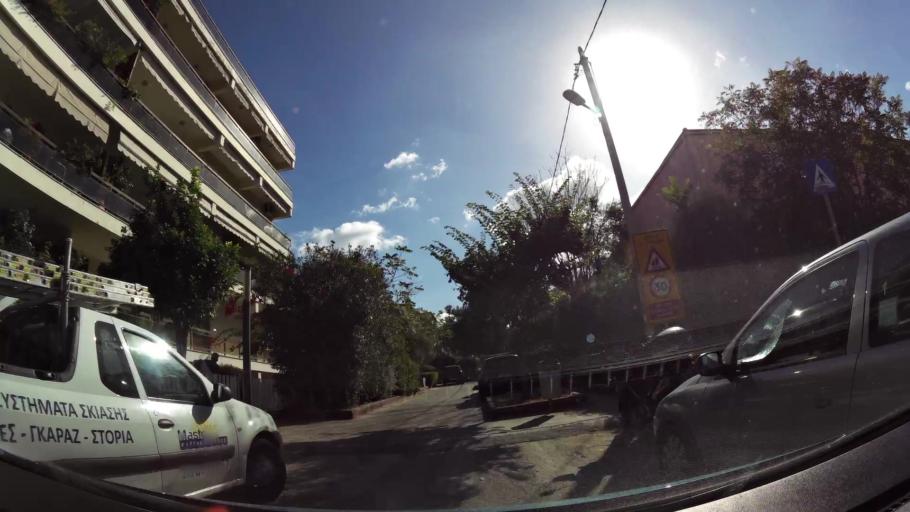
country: GR
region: Attica
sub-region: Nomarchia Athinas
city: Neo Psychiko
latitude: 38.0044
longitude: 23.7787
